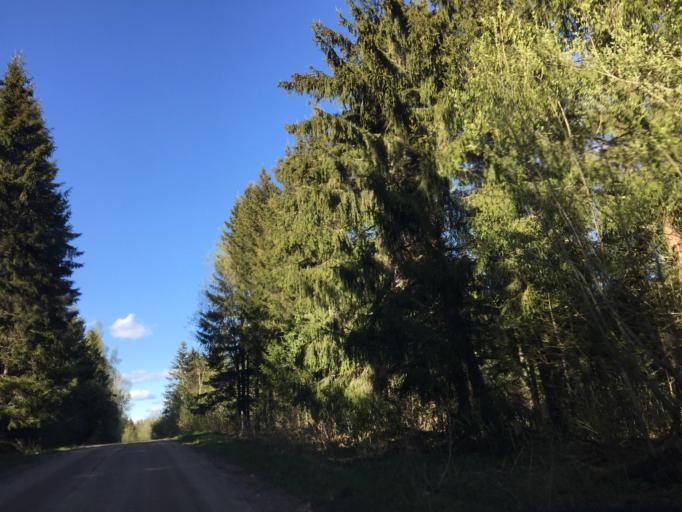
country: LV
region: Vecpiebalga
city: Vecpiebalga
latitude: 56.8598
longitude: 25.9645
